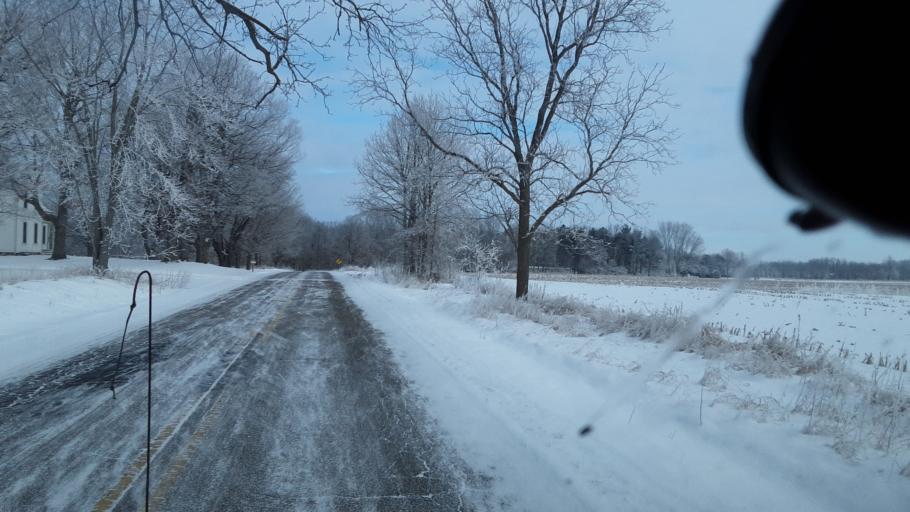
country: US
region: Michigan
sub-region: Ingham County
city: Leslie
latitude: 42.3906
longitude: -84.4924
